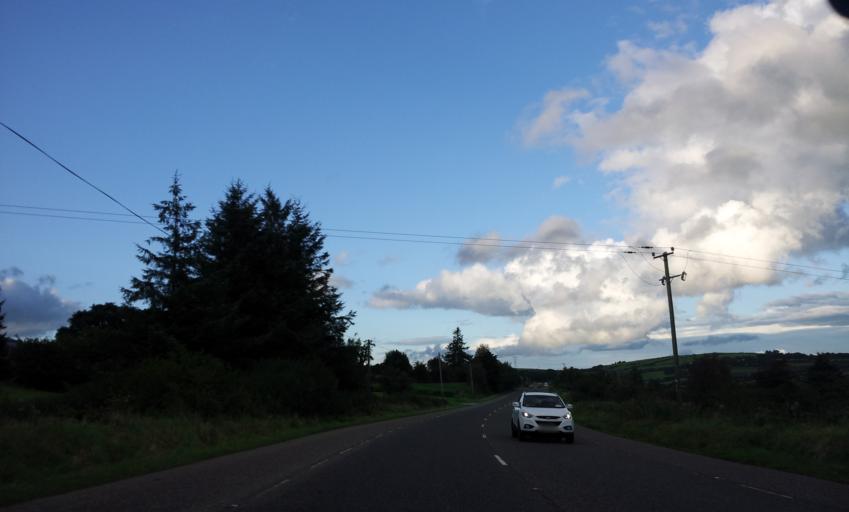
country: IE
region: Munster
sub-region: Ciarrai
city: Castleisland
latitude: 52.3028
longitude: -9.3815
